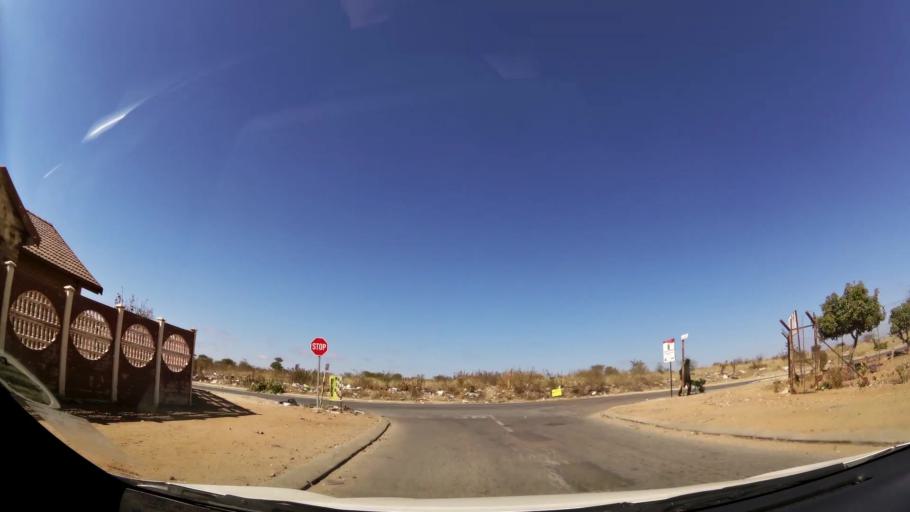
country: ZA
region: Limpopo
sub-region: Capricorn District Municipality
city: Polokwane
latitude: -23.8753
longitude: 29.4148
